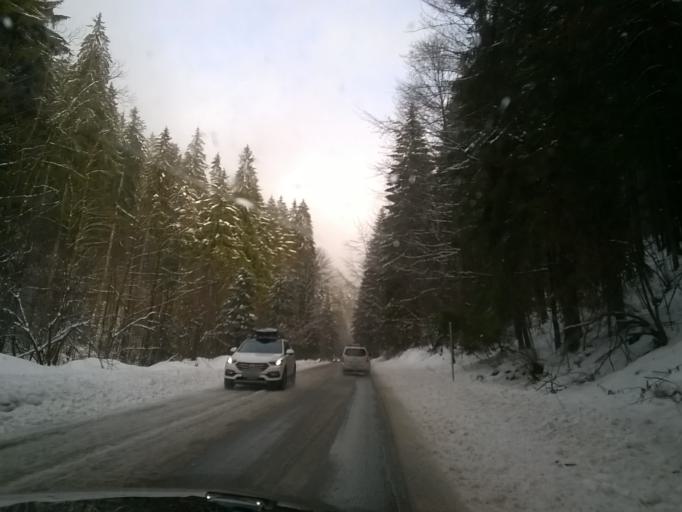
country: SK
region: Banskobystricky
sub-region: Okres Ziar nad Hronom
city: Kremnica
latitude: 48.7154
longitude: 18.9583
